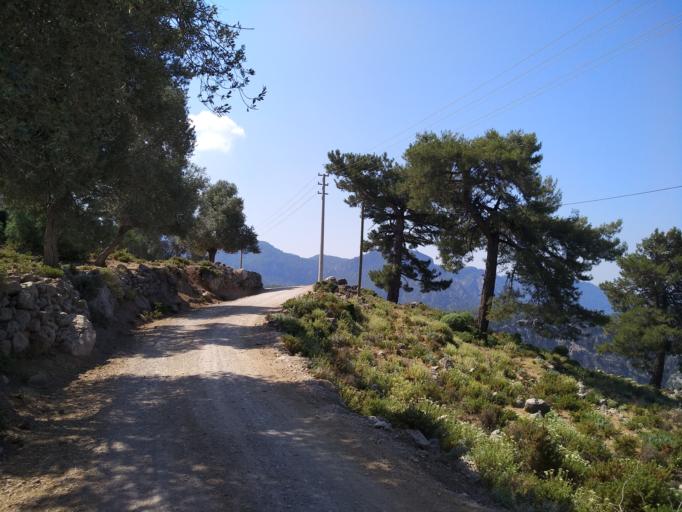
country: TR
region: Mugla
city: OEluedeniz
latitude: 36.5258
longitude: 29.1504
